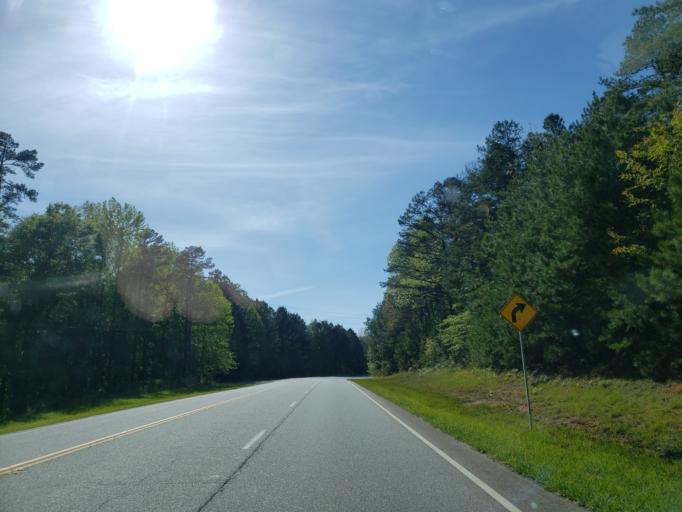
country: US
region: Georgia
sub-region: Haralson County
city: Tallapoosa
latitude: 33.7146
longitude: -85.2769
